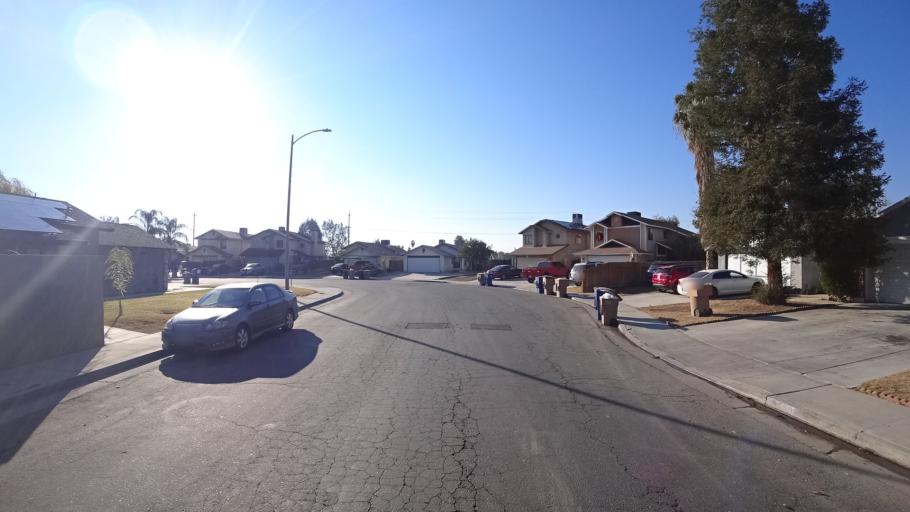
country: US
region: California
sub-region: Kern County
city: Greenfield
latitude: 35.2968
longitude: -119.0158
